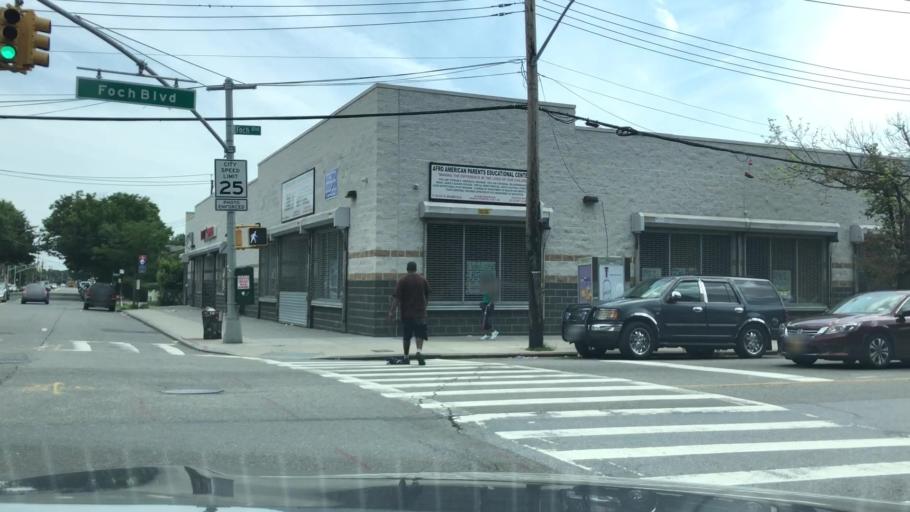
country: US
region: New York
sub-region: Queens County
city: Jamaica
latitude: 40.6843
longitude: -73.7831
